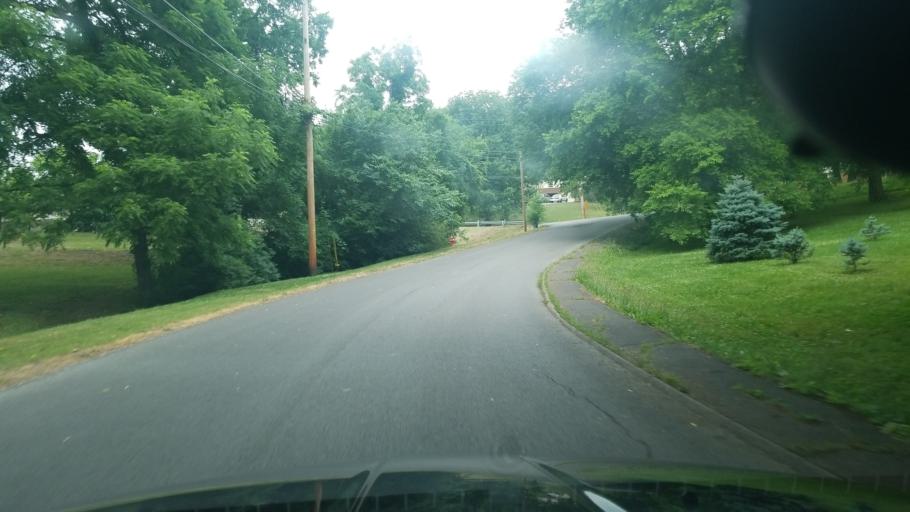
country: US
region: Tennessee
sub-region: Davidson County
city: Goodlettsville
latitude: 36.2576
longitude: -86.7413
